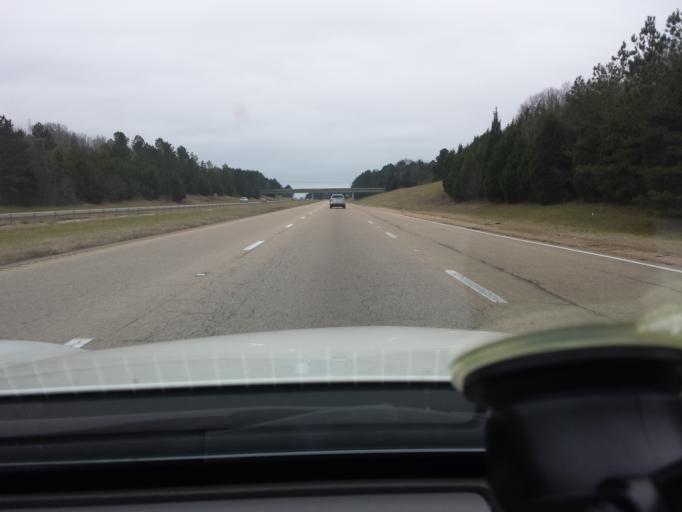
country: US
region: Mississippi
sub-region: Lee County
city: Verona
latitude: 34.1879
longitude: -88.7066
